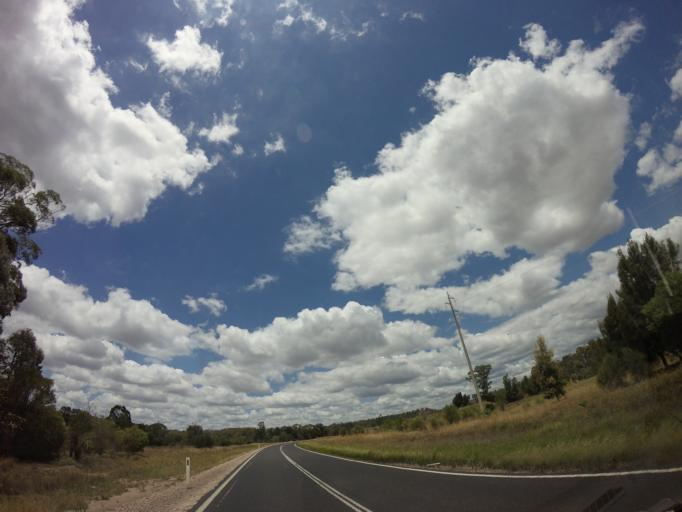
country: AU
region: Queensland
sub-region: Goondiwindi
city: Goondiwindi
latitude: -28.0388
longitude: 150.8025
